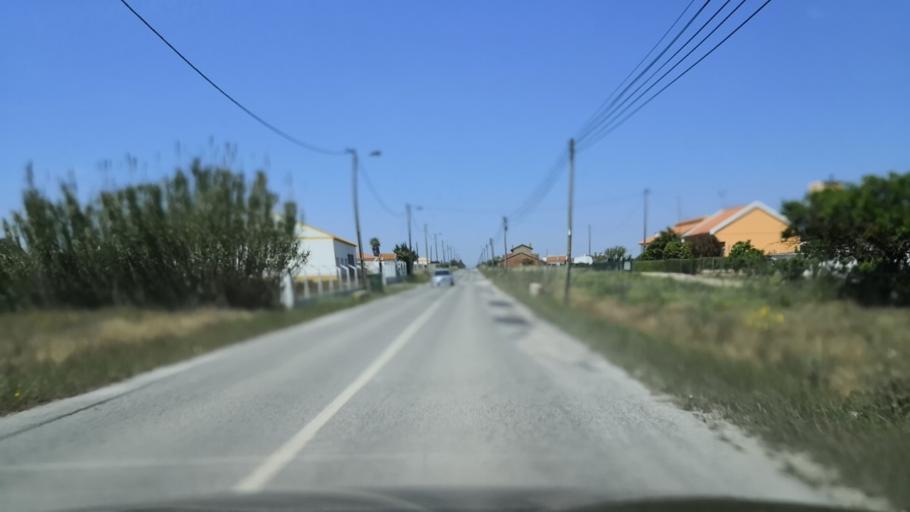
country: PT
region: Setubal
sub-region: Palmela
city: Pinhal Novo
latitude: 38.6391
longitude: -8.7423
